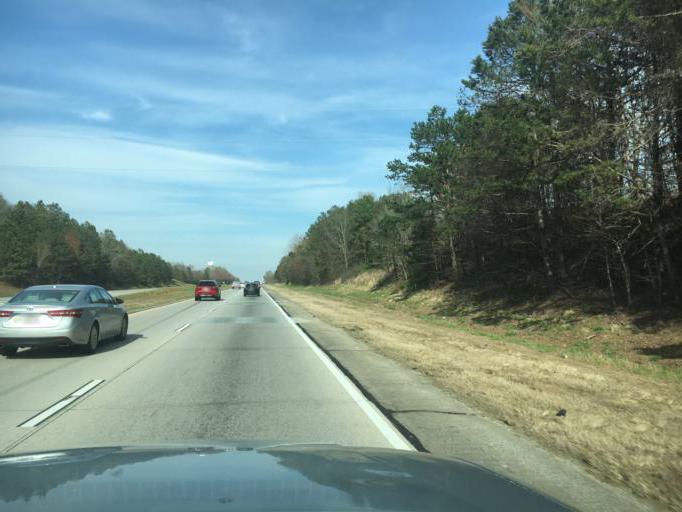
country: US
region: Georgia
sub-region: Hall County
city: Lula
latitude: 34.3890
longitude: -83.7012
